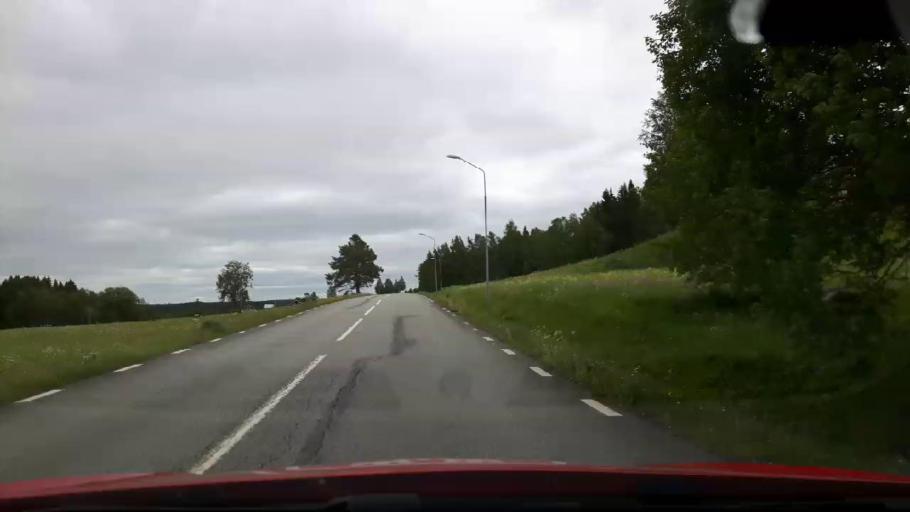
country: SE
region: Jaemtland
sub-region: Stroemsunds Kommun
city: Stroemsund
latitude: 63.5688
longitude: 15.3894
